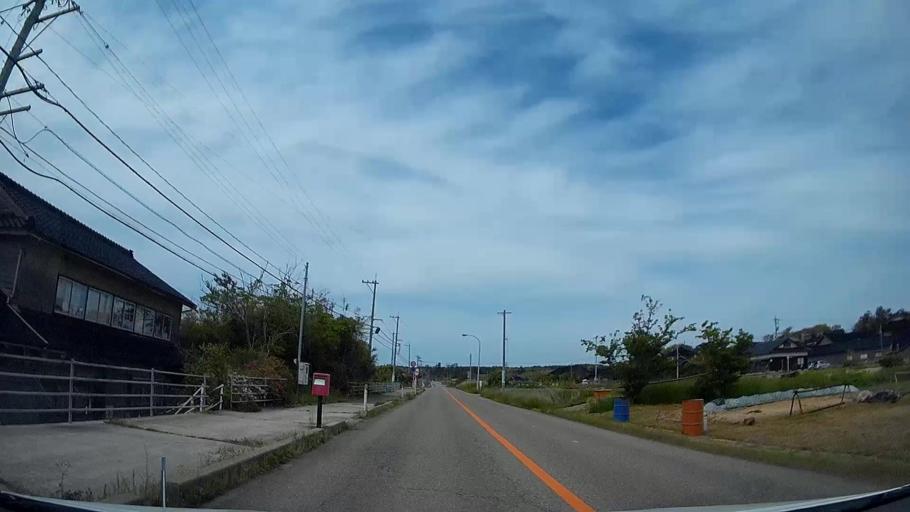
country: JP
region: Ishikawa
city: Hakui
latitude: 37.0295
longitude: 136.7474
